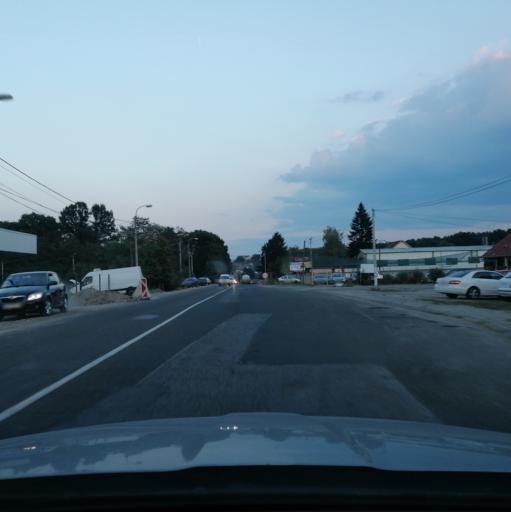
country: RS
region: Central Serbia
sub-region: Raski Okrug
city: Kraljevo
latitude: 43.7025
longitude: 20.7298
